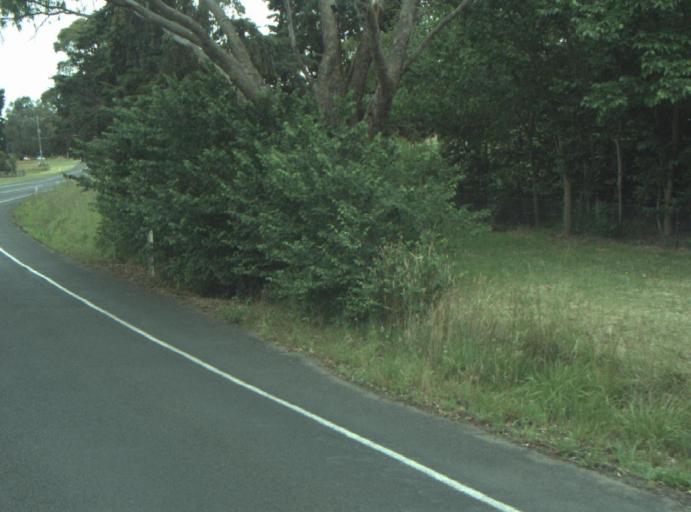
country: AU
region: Victoria
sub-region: Greater Geelong
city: Leopold
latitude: -38.2130
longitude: 144.5070
